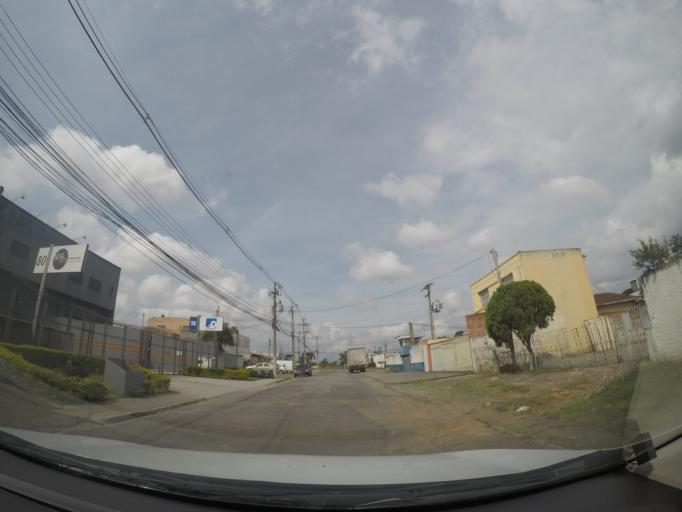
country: BR
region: Parana
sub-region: Curitiba
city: Curitiba
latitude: -25.4896
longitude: -49.2723
